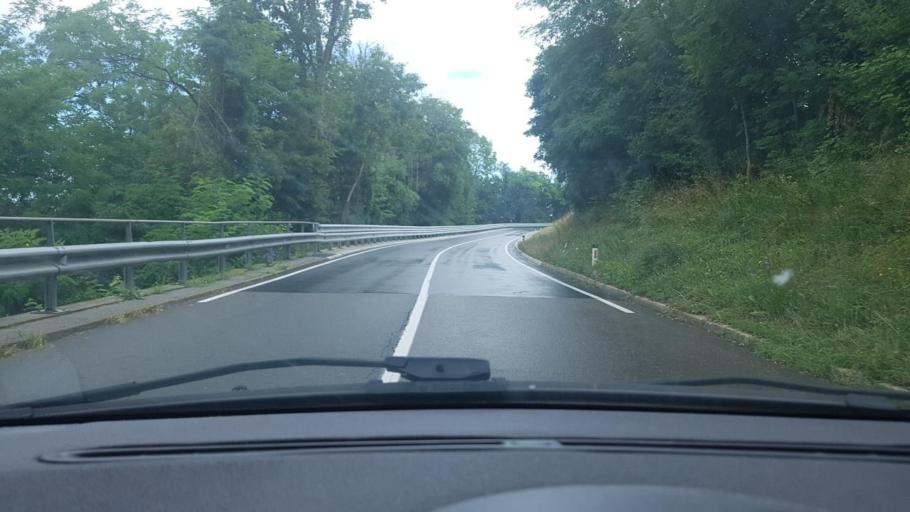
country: AT
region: Styria
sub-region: Politischer Bezirk Suedoststeiermark
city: Mureck
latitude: 46.7035
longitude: 15.7853
